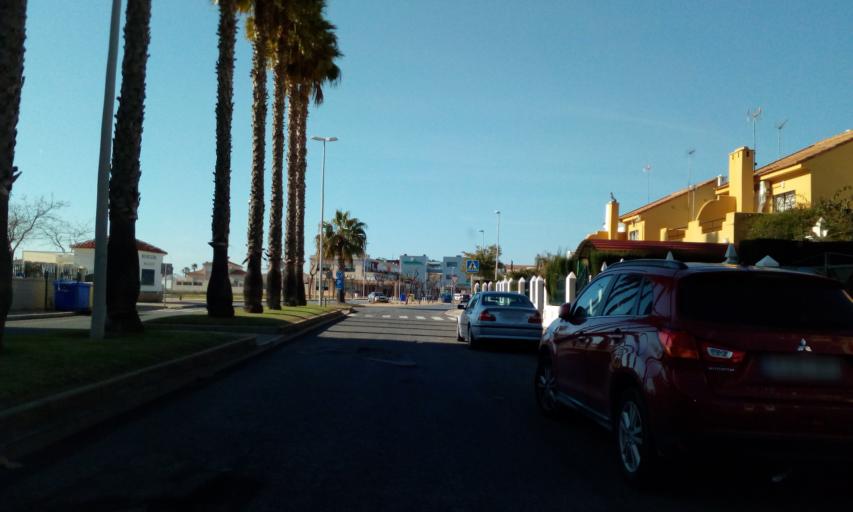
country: ES
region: Andalusia
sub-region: Provincia de Huelva
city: Lepe
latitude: 37.2071
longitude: -7.2238
